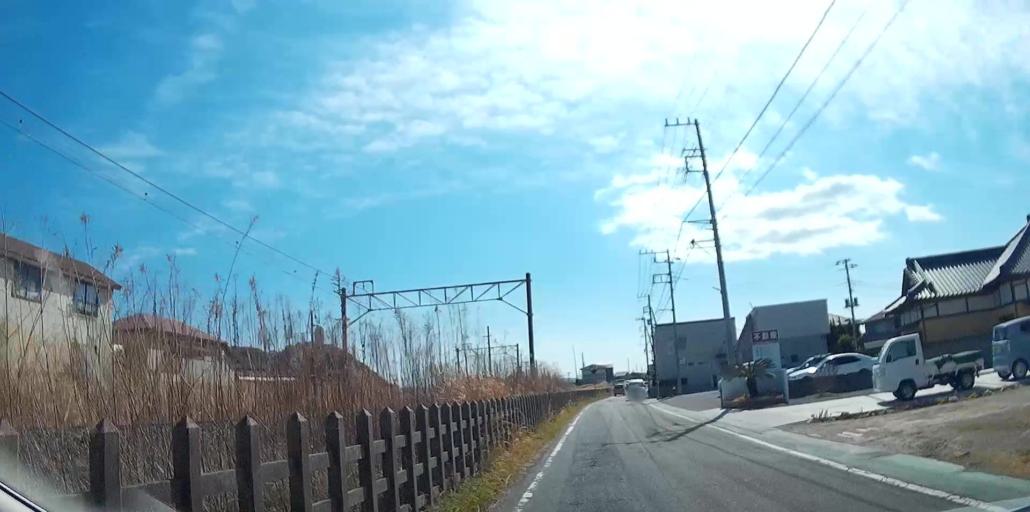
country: JP
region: Chiba
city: Tateyama
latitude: 35.0303
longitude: 139.8504
